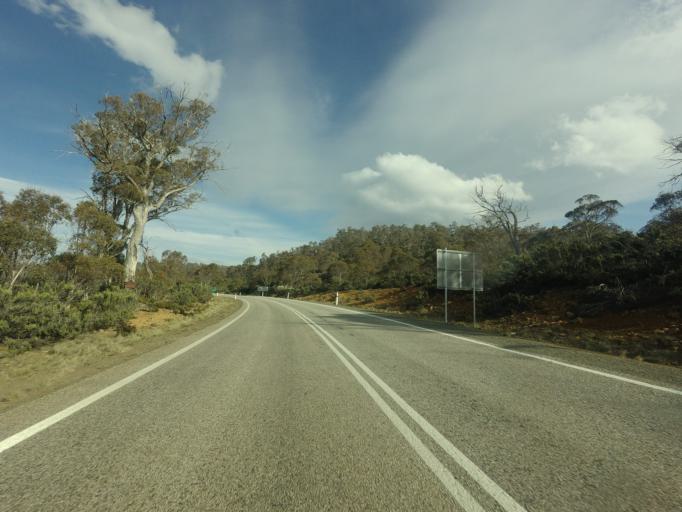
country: AU
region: Tasmania
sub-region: Meander Valley
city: Deloraine
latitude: -41.9817
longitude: 146.6790
